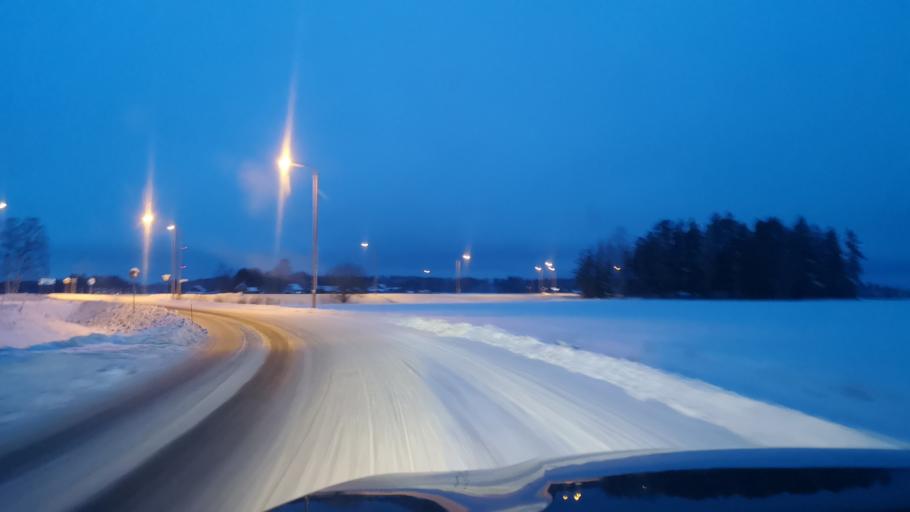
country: FI
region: Varsinais-Suomi
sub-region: Loimaa
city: Loimaa
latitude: 60.8838
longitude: 23.0893
